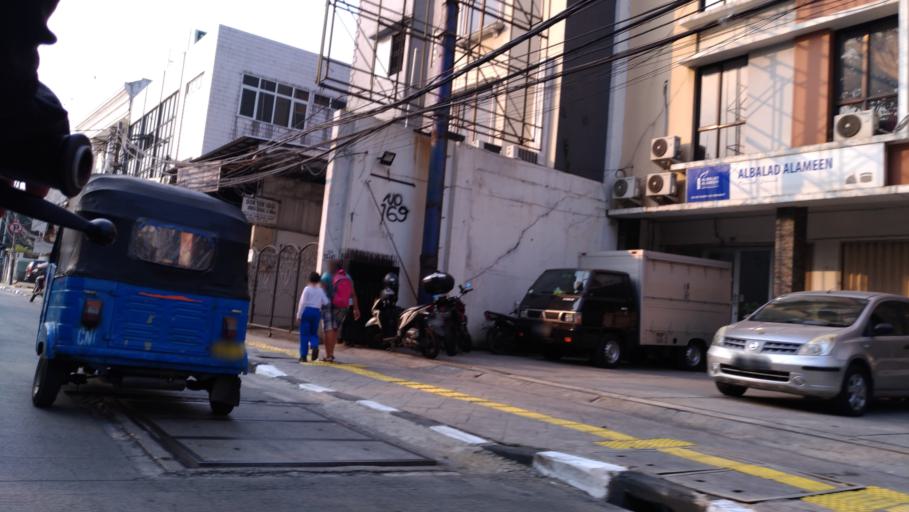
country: ID
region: Jakarta Raya
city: Jakarta
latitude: -6.2224
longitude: 106.8658
